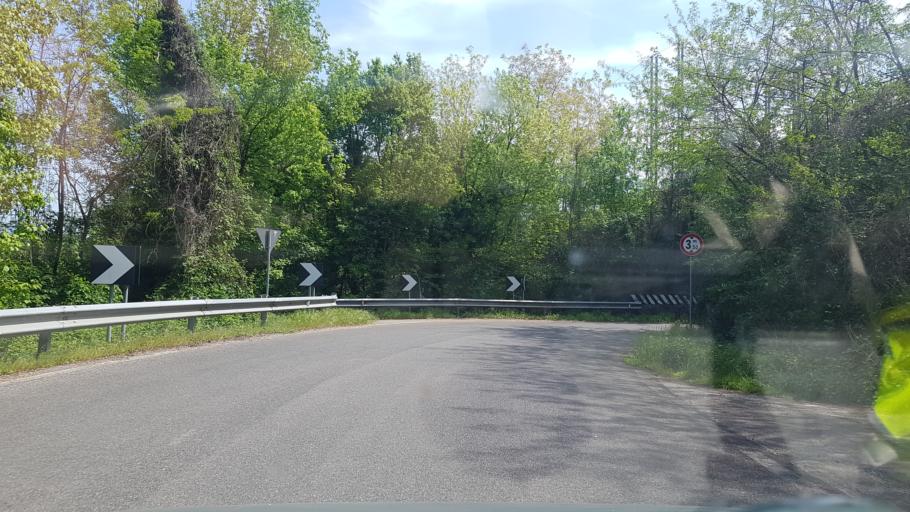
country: IT
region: Friuli Venezia Giulia
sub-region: Provincia di Gorizia
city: Savogna d'Isonzo
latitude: 45.8989
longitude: 13.5663
